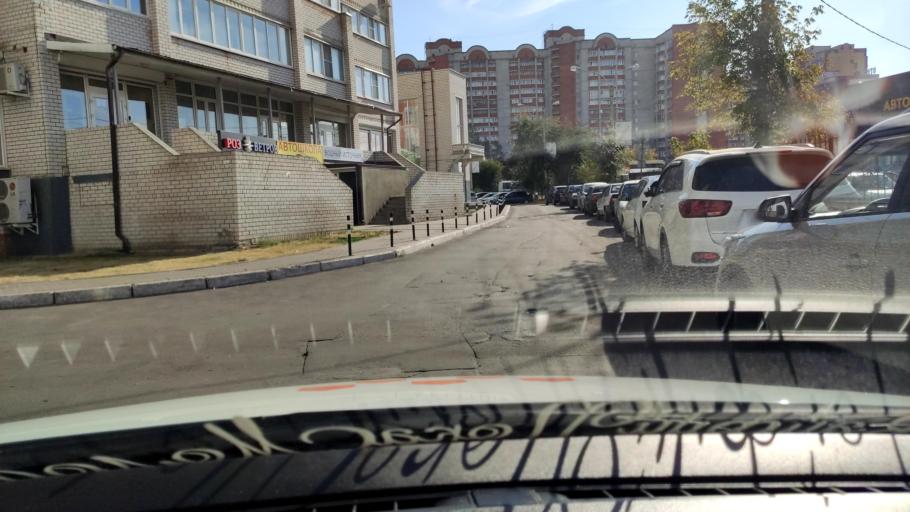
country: RU
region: Voronezj
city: Podgornoye
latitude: 51.7140
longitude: 39.1437
